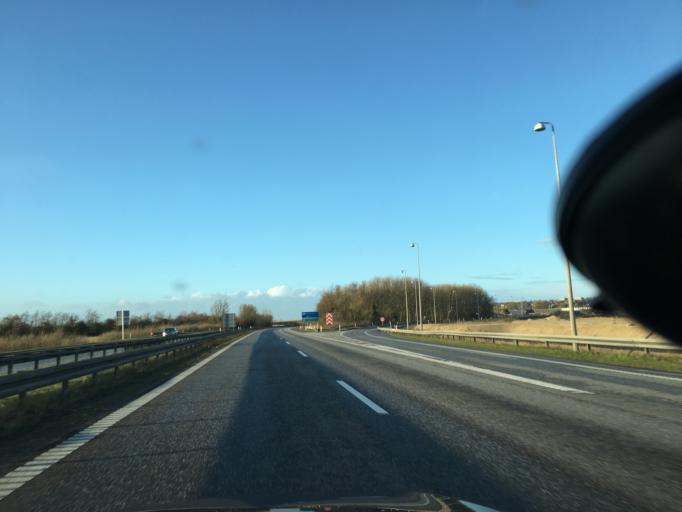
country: DK
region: North Denmark
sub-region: Alborg Kommune
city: Aalborg
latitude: 57.0020
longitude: 9.9086
